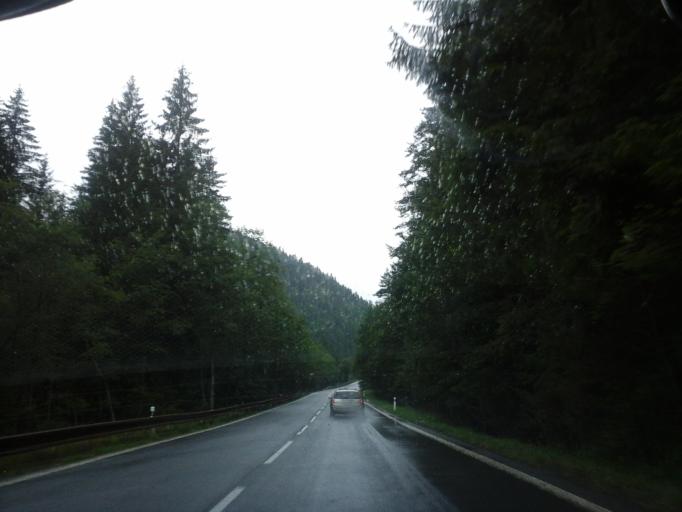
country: SK
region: Kosicky
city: Dobsina
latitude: 48.8737
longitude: 20.2700
